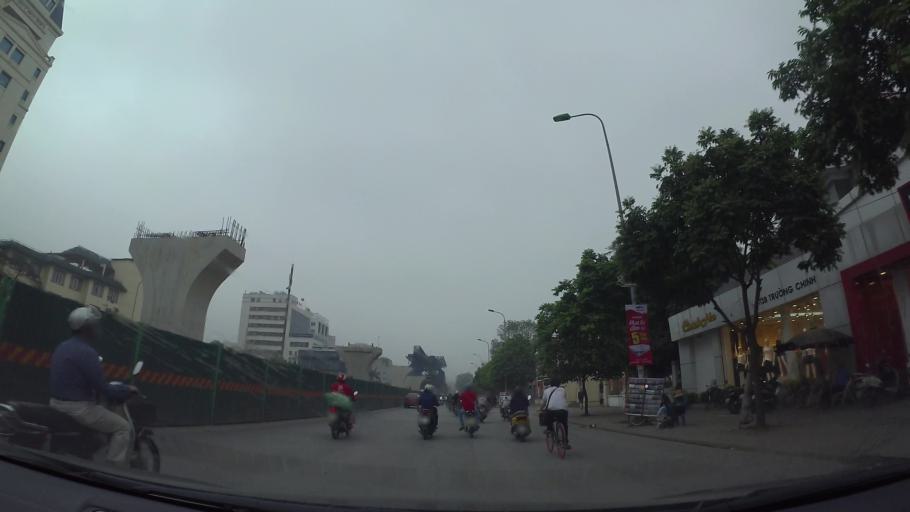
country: VN
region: Ha Noi
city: Dong Da
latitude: 21.0001
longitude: 105.8305
